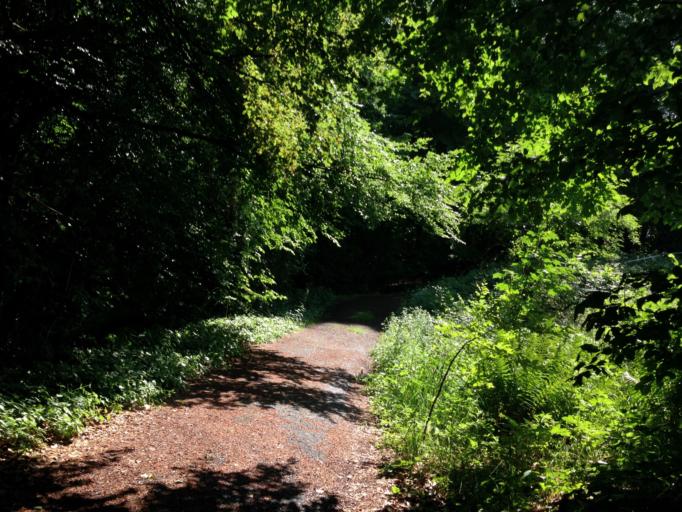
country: DE
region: Hesse
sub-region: Regierungsbezirk Giessen
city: Marburg an der Lahn
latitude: 50.8498
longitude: 8.7548
